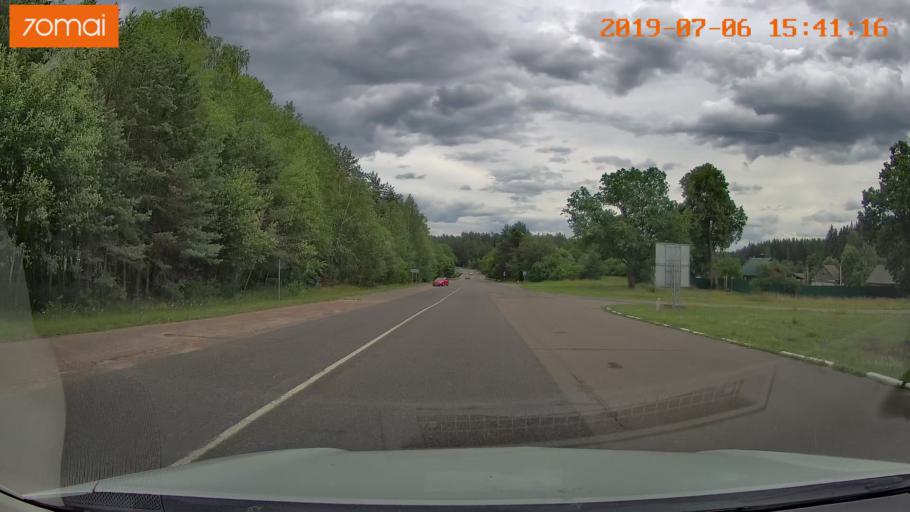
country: BY
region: Minsk
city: Rakaw
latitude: 53.9854
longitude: 26.9829
